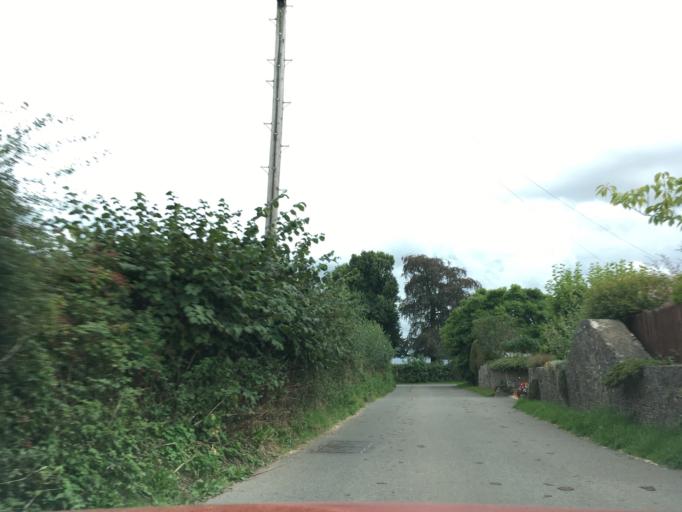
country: GB
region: Wales
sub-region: Monmouthshire
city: Chepstow
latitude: 51.6167
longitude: -2.6886
